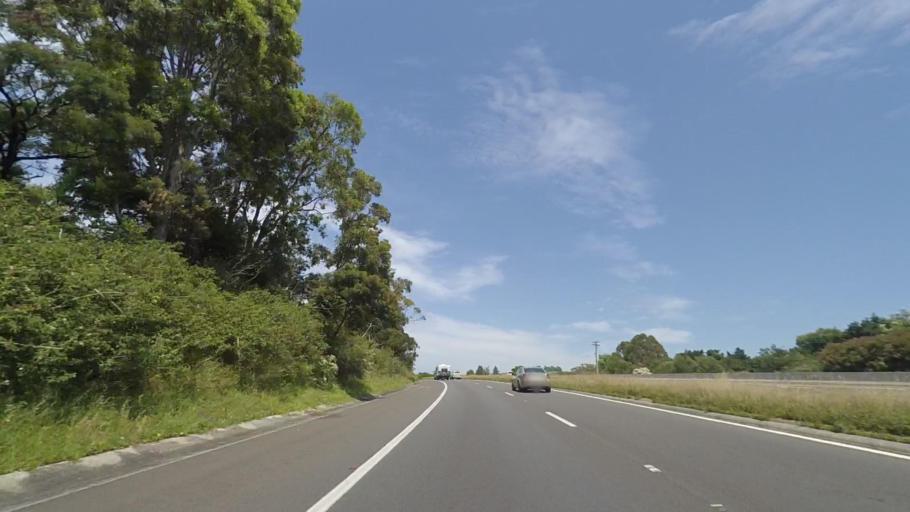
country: AU
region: New South Wales
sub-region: Kiama
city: Kiama
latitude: -34.6725
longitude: 150.8429
